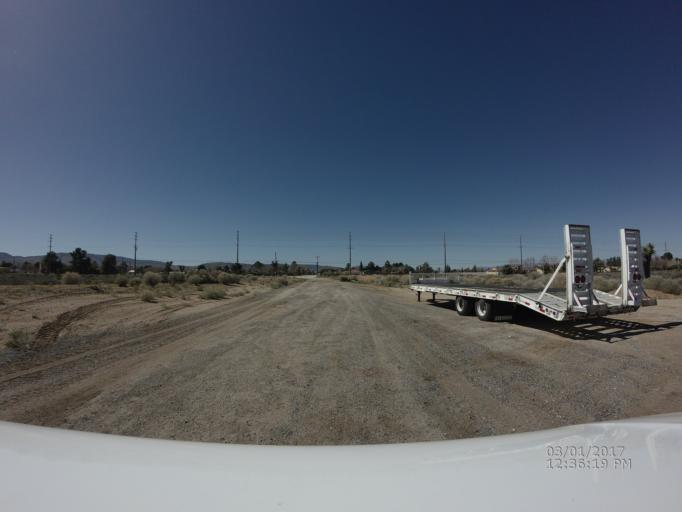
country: US
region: California
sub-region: Los Angeles County
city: Desert View Highlands
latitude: 34.6387
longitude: -118.1643
